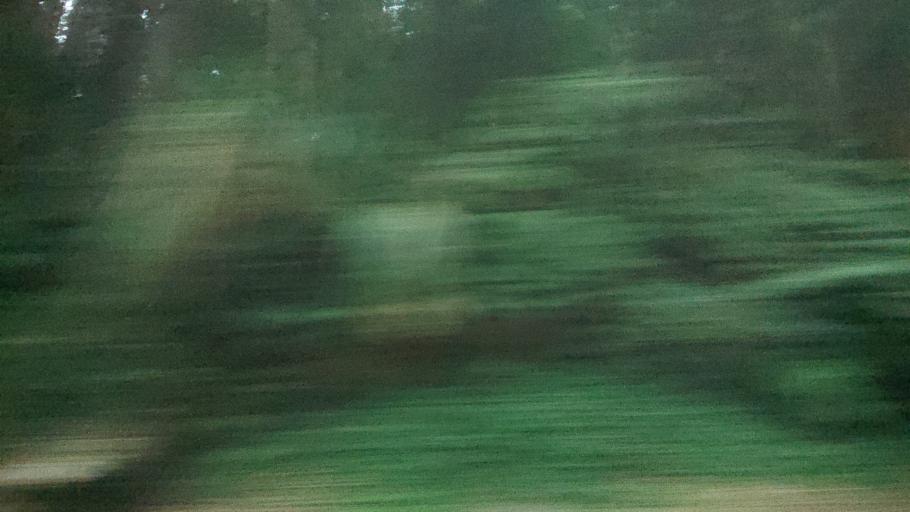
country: TW
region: Taiwan
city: Lugu
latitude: 23.5046
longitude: 120.7010
